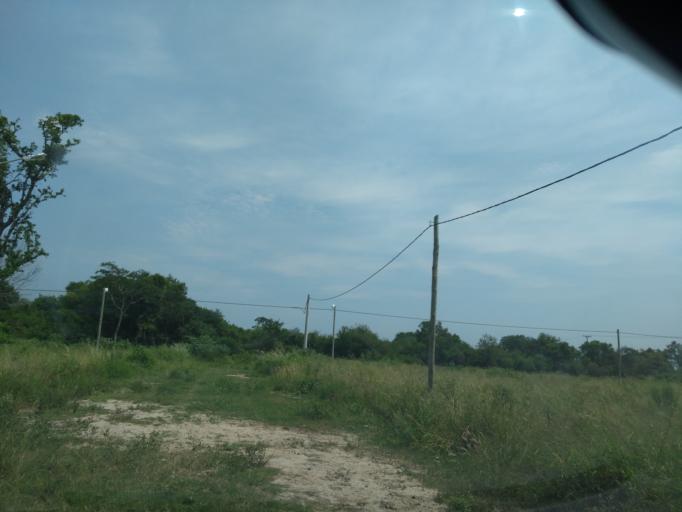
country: AR
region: Chaco
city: Fontana
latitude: -27.4066
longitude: -58.9708
